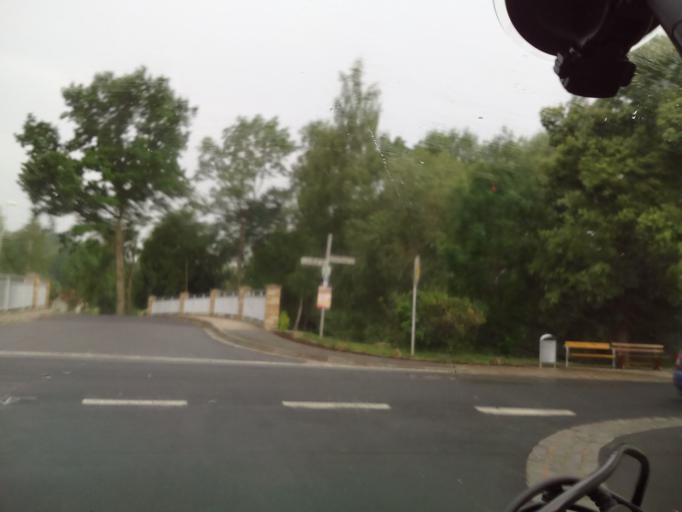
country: DE
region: Bavaria
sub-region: Regierungsbezirk Unterfranken
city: Hochheim
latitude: 50.3633
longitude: 10.4499
